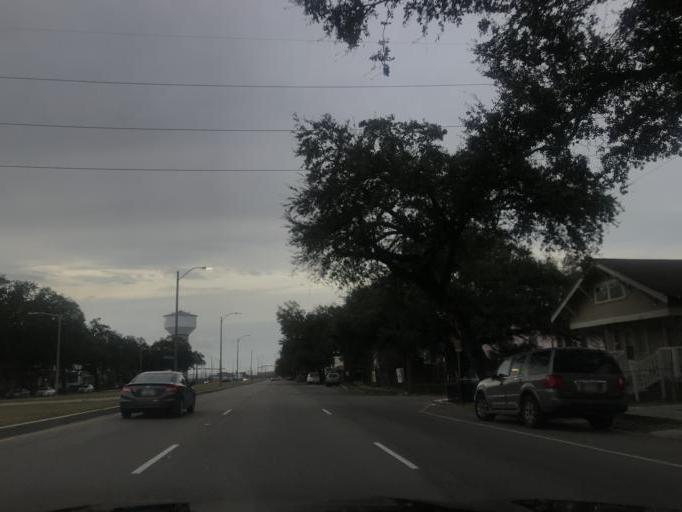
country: US
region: Louisiana
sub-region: Jefferson Parish
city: Jefferson
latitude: 29.9579
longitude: -90.1228
